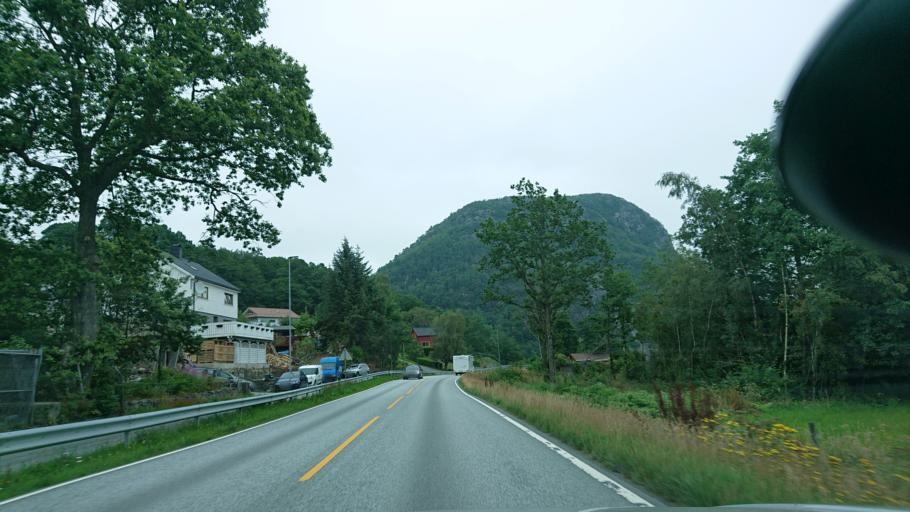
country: NO
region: Rogaland
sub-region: Strand
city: Tau
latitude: 59.0670
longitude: 5.9488
